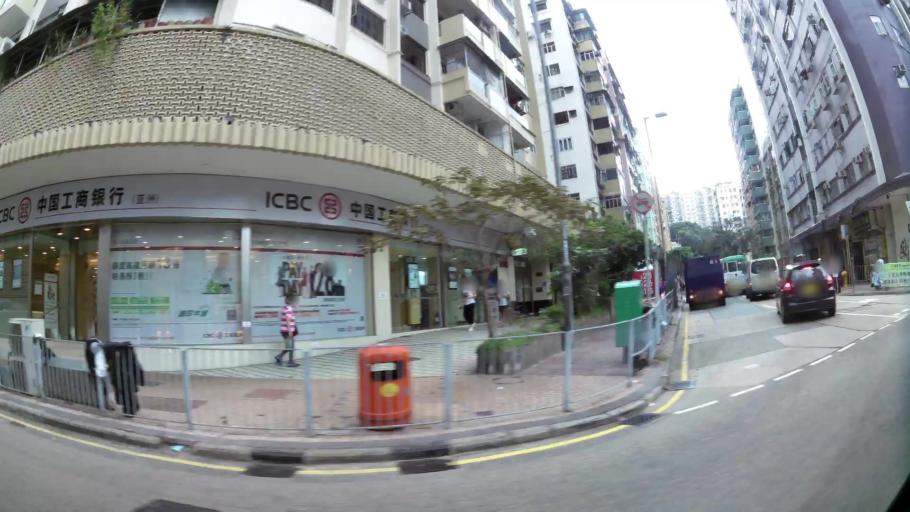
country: HK
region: Kowloon City
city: Kowloon
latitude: 22.3174
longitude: 114.1747
